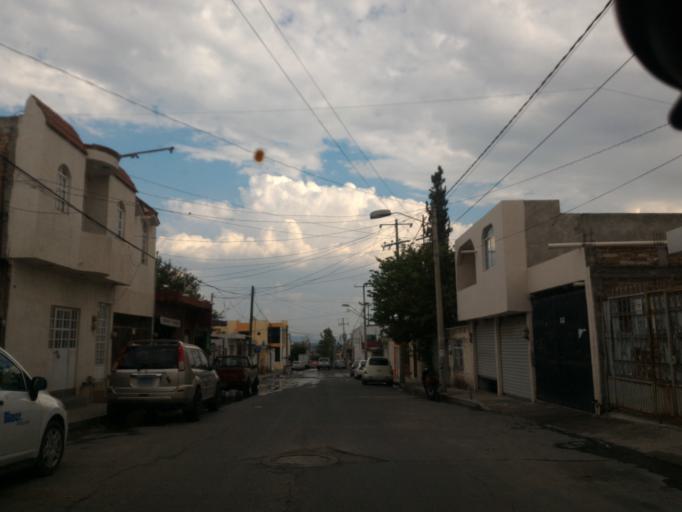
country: MX
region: Guanajuato
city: San Francisco del Rincon
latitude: 21.0414
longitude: -101.8565
